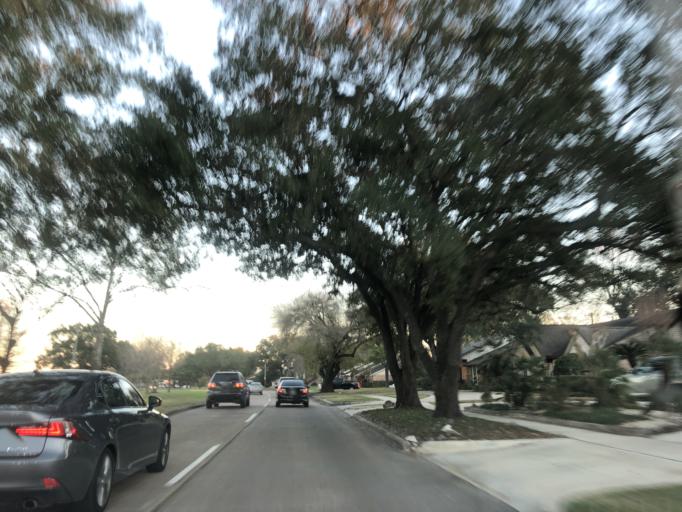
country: US
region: Texas
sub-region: Harris County
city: Bellaire
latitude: 29.6756
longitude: -95.4897
